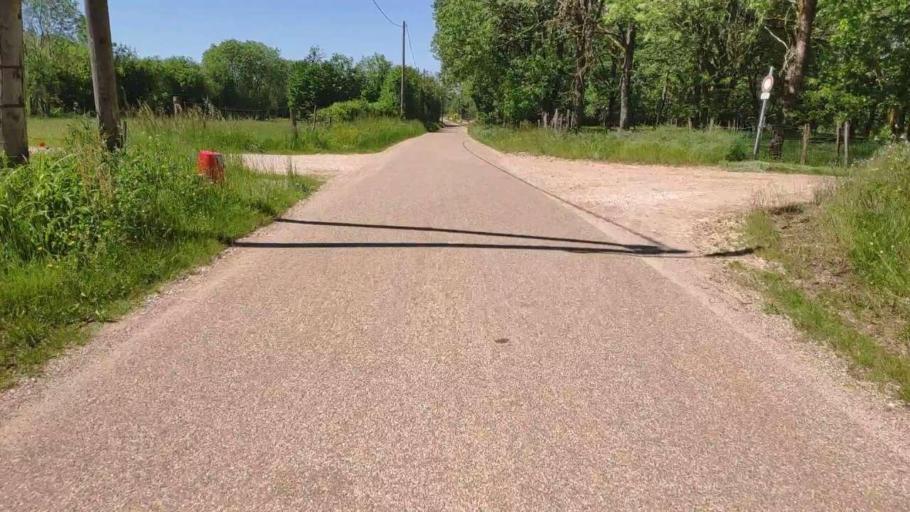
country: FR
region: Franche-Comte
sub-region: Departement du Jura
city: Poligny
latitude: 46.7294
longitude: 5.7519
